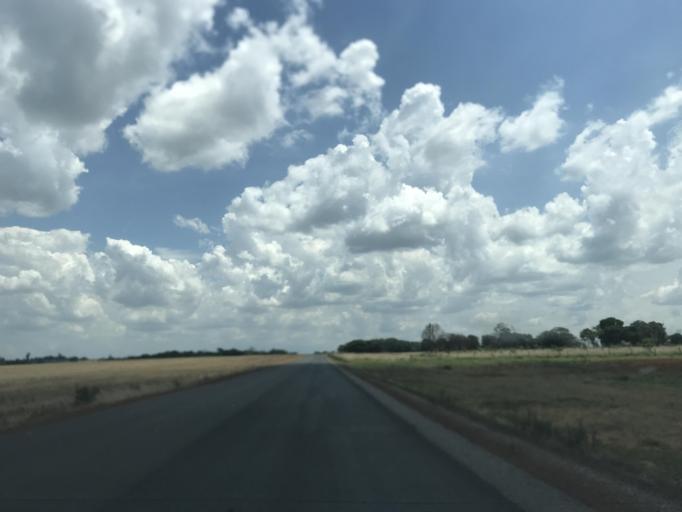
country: BR
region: Goias
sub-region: Piracanjuba
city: Piracanjuba
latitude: -17.3180
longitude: -48.8004
